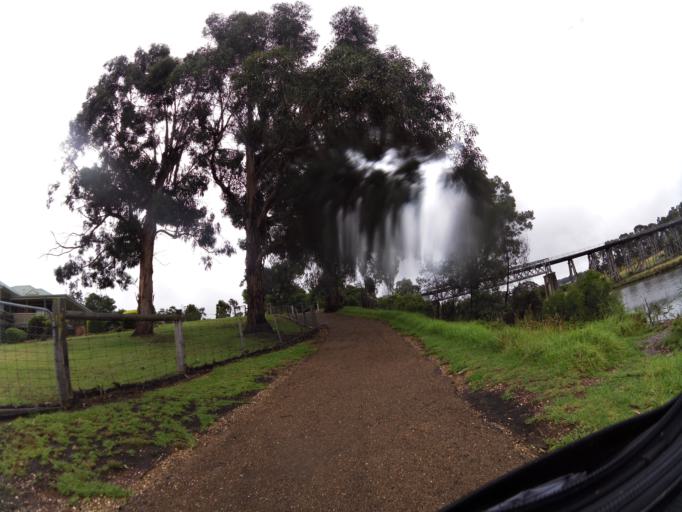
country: AU
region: Victoria
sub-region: East Gippsland
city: Bairnsdale
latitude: -37.8141
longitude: 147.7394
